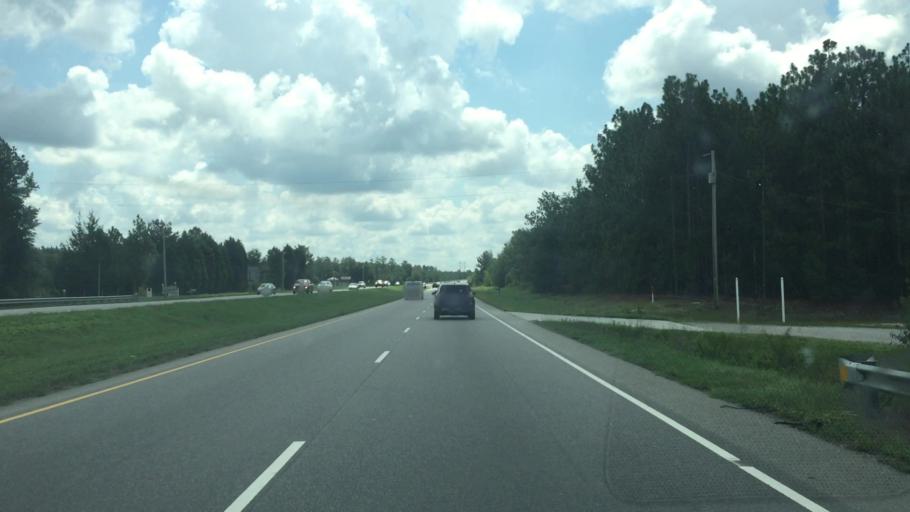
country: US
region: North Carolina
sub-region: Scotland County
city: Laurel Hill
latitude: 34.8397
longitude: -79.6019
